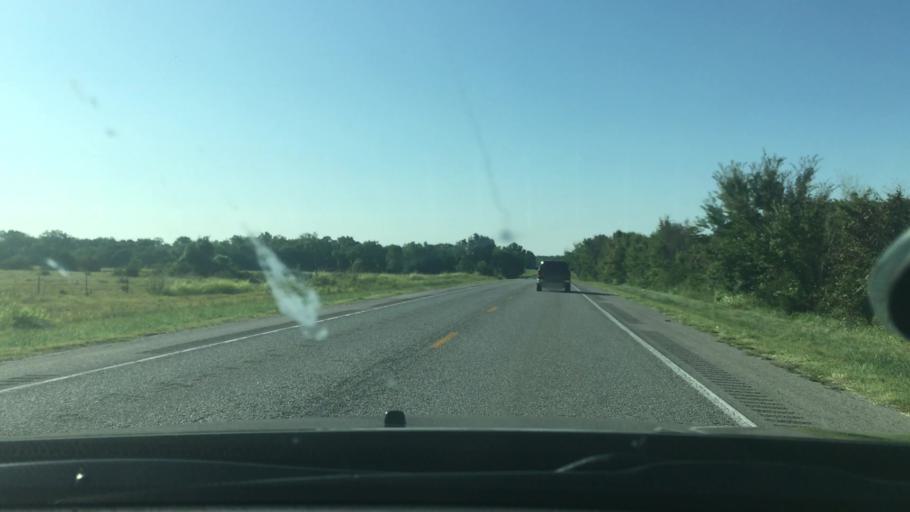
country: US
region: Oklahoma
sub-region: Johnston County
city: Tishomingo
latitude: 34.2543
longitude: -96.7634
